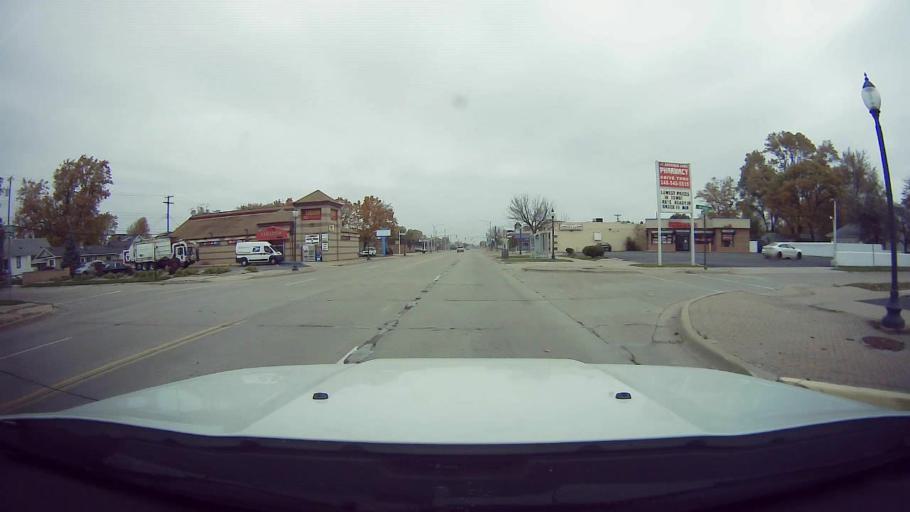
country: US
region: Michigan
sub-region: Oakland County
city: Madison Heights
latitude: 42.4747
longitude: -83.1044
